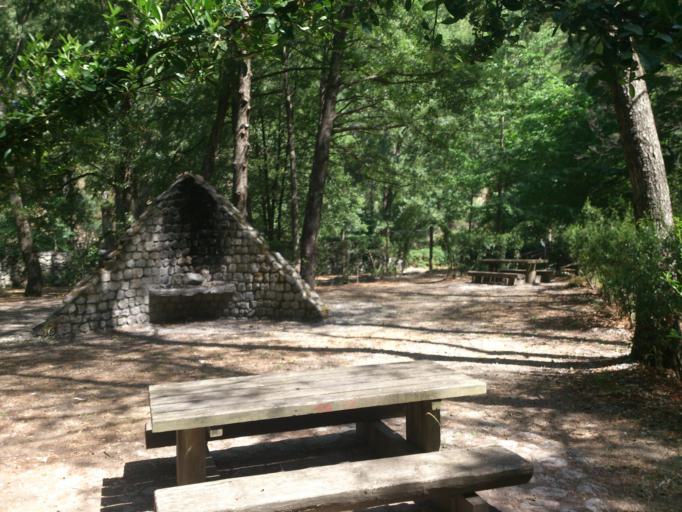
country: IT
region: Calabria
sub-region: Provincia di Reggio Calabria
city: Bivongi
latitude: 38.4867
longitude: 16.4325
